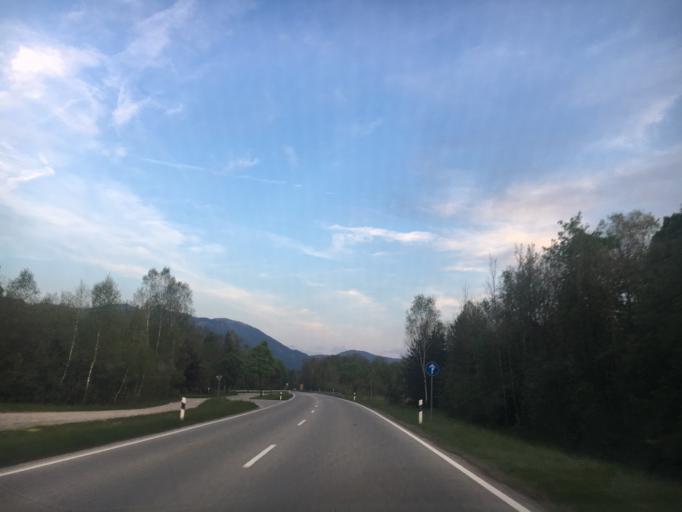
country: DE
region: Bavaria
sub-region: Upper Bavaria
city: Lenggries
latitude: 47.6908
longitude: 11.5668
